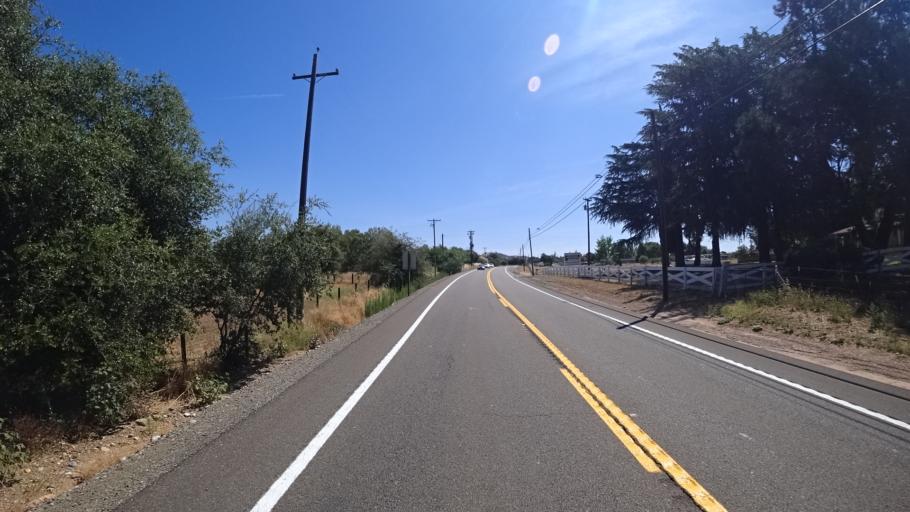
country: US
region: California
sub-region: Calaveras County
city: Rancho Calaveras
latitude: 38.1825
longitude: -120.9019
